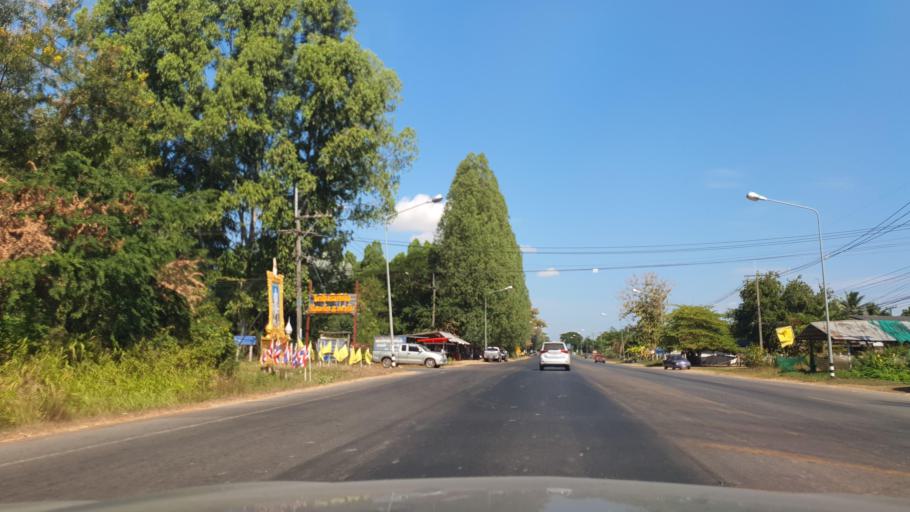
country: TH
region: Kalasin
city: Somdet
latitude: 16.7241
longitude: 103.7600
